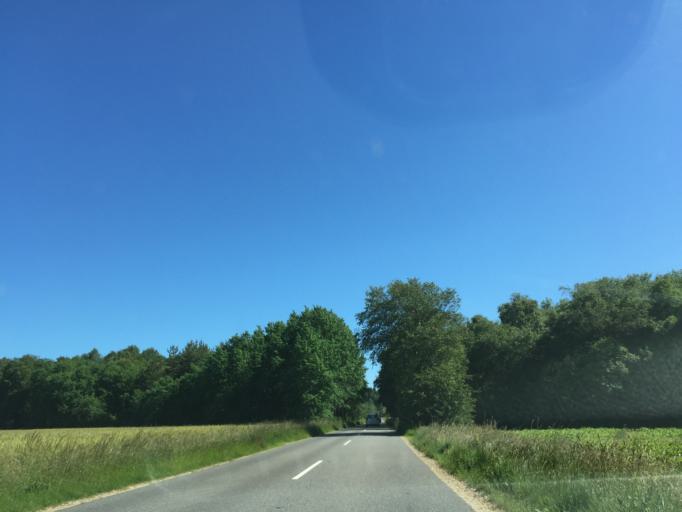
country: DK
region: Central Jutland
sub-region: Viborg Kommune
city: Bjerringbro
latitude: 56.2926
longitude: 9.6736
